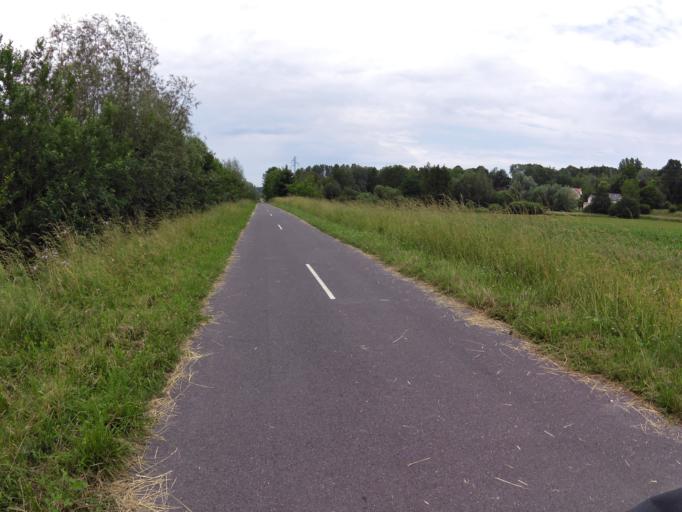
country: FR
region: Champagne-Ardenne
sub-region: Departement des Ardennes
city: Lumes
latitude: 49.7468
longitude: 4.7759
